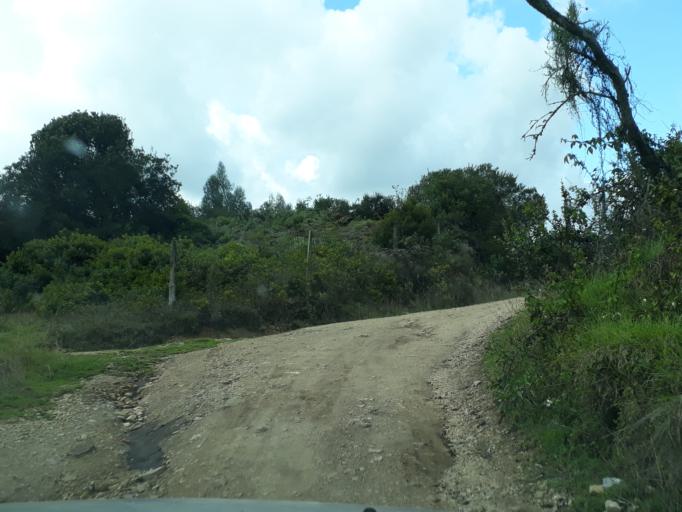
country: CO
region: Cundinamarca
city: Lenguazaque
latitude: 5.2697
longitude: -73.6868
